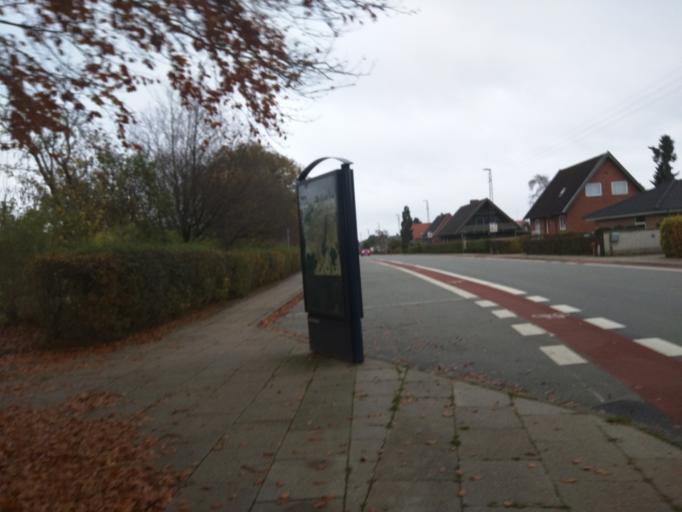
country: DK
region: Central Jutland
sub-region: Viborg Kommune
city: Viborg
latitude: 56.4589
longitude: 9.3869
